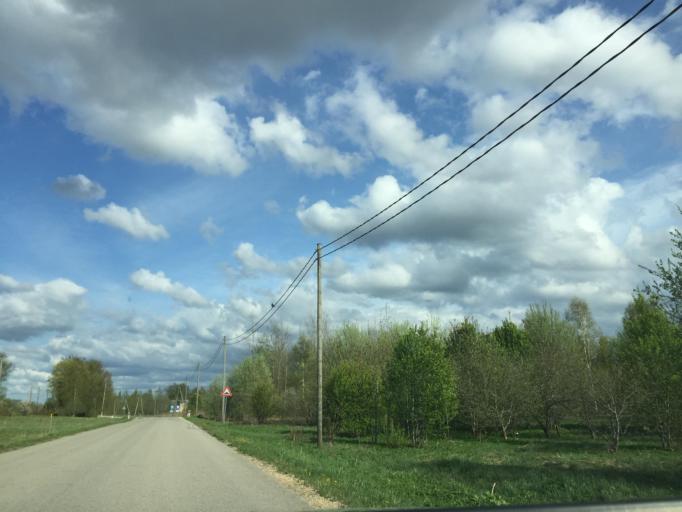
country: LV
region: Sigulda
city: Sigulda
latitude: 57.1320
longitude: 24.8423
